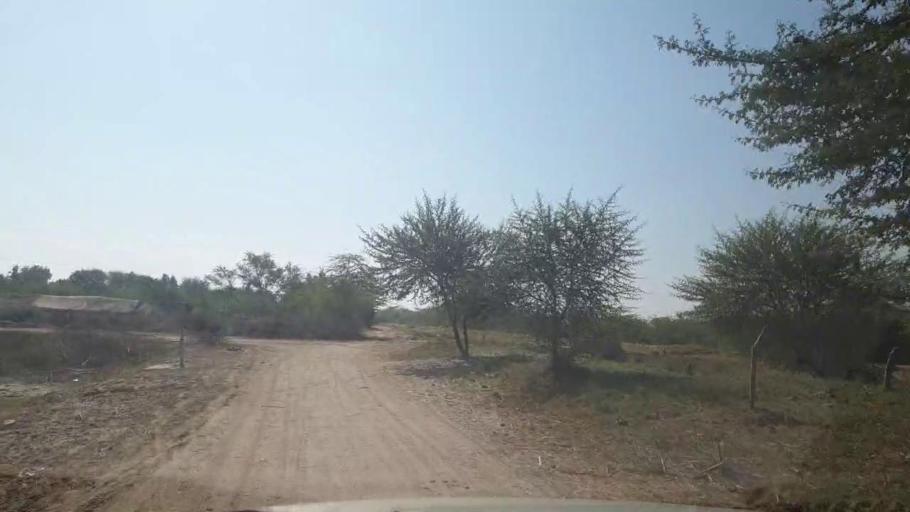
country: PK
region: Sindh
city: Mirpur Khas
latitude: 25.5131
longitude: 69.1575
